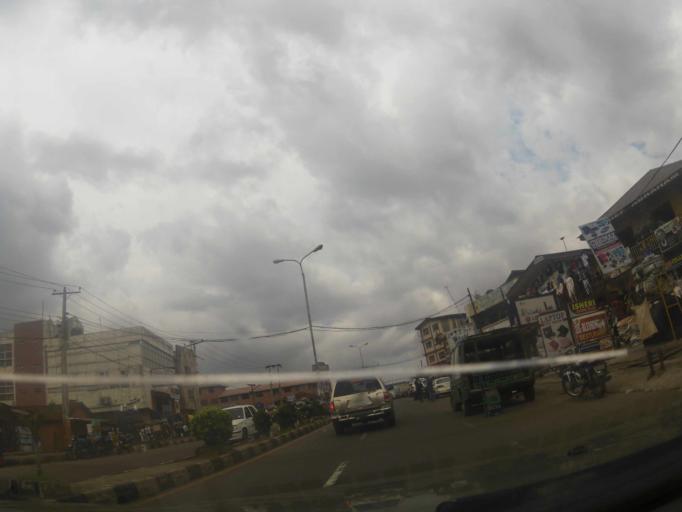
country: NG
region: Oyo
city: Ibadan
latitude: 7.3923
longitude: 3.8822
